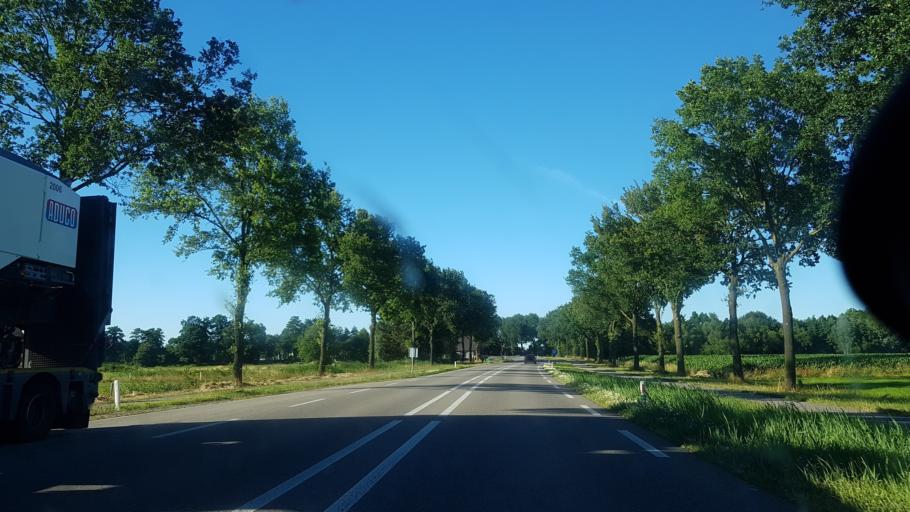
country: NL
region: Gelderland
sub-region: Gemeente Apeldoorn
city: Loenen
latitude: 52.1587
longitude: 6.0539
